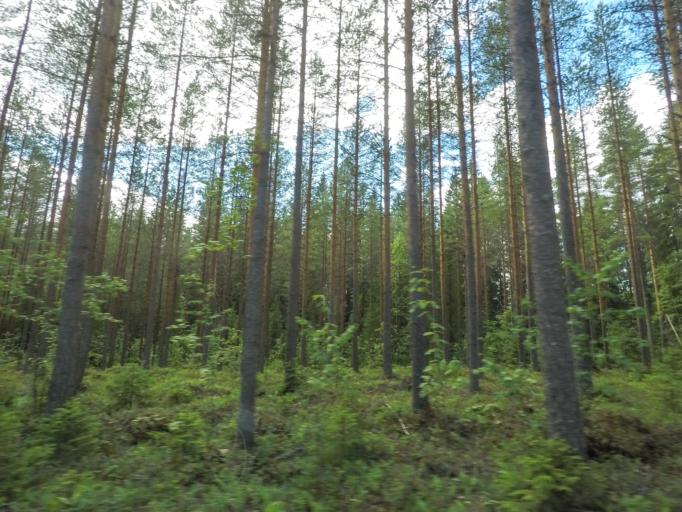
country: FI
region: Central Finland
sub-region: Jyvaeskylae
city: Hankasalmi
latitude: 62.4119
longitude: 26.6441
